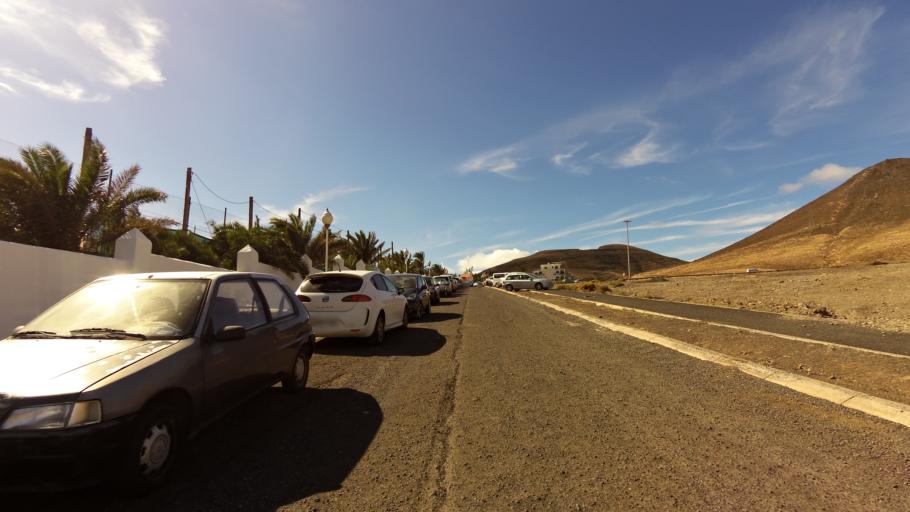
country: ES
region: Canary Islands
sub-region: Provincia de Las Palmas
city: Pajara
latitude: 28.0609
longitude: -14.3155
